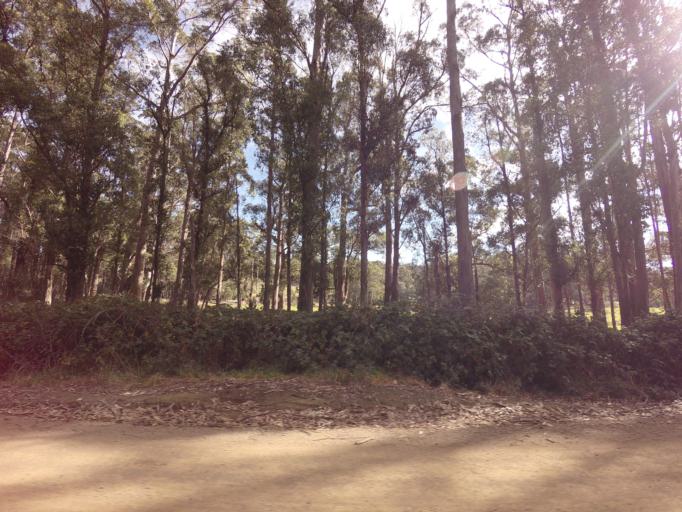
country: AU
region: Tasmania
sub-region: Clarence
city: Sandford
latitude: -43.1520
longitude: 147.7634
